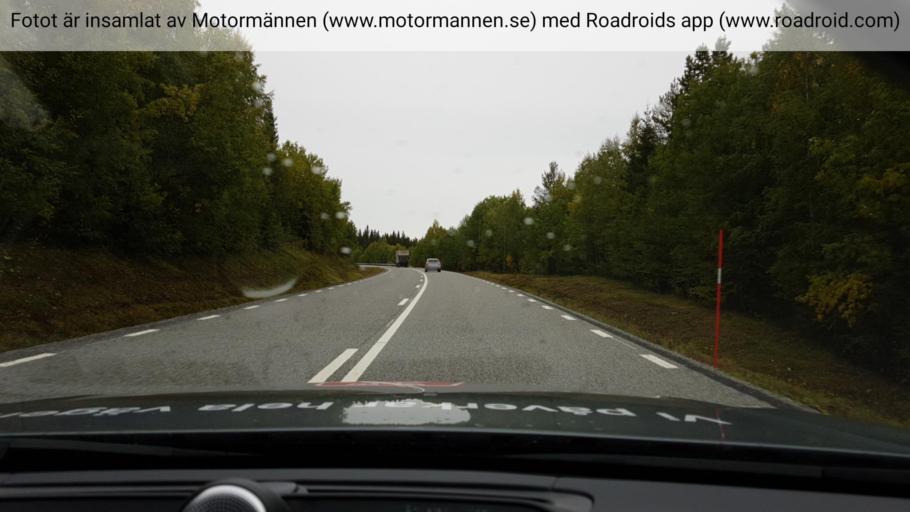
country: SE
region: Jaemtland
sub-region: Stroemsunds Kommun
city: Stroemsund
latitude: 64.0834
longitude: 15.5657
